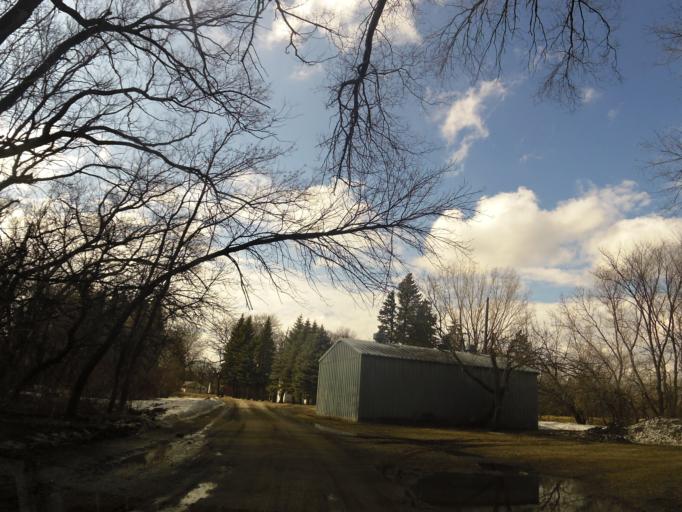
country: US
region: North Dakota
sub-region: Walsh County
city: Grafton
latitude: 48.4220
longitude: -97.3928
